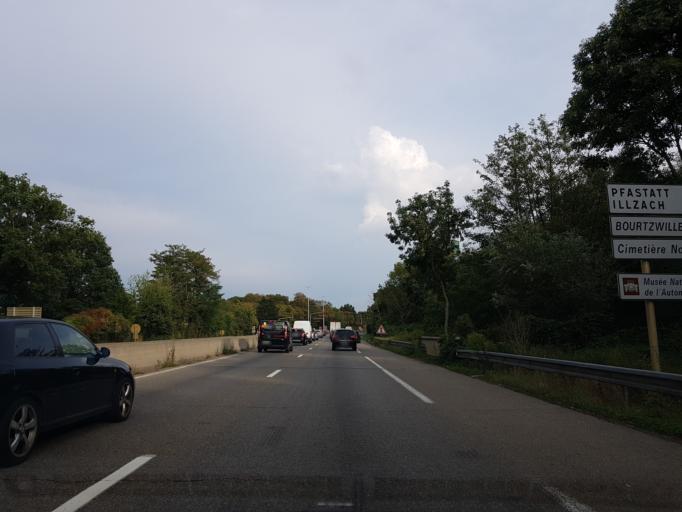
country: FR
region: Alsace
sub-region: Departement du Haut-Rhin
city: Kingersheim
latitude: 47.7823
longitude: 7.3277
